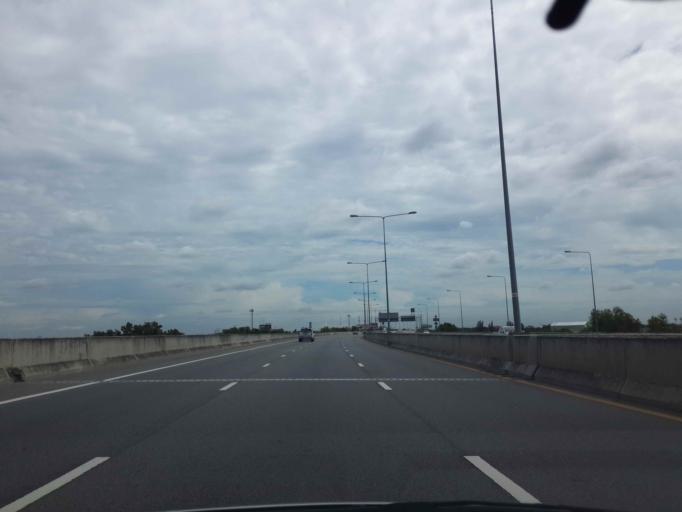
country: TH
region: Bangkok
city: Bang Khen
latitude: 13.8891
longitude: 100.6536
